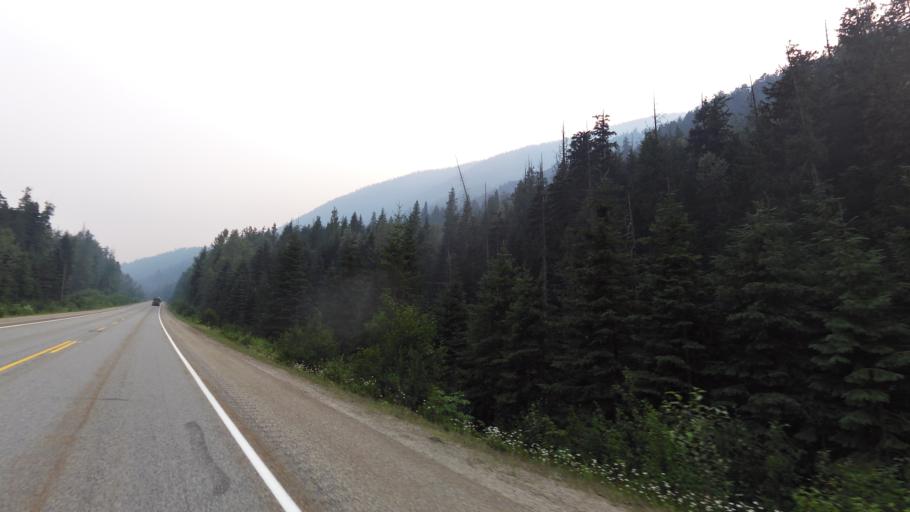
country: CA
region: Alberta
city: Jasper Park Lodge
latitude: 52.3138
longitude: -119.1792
